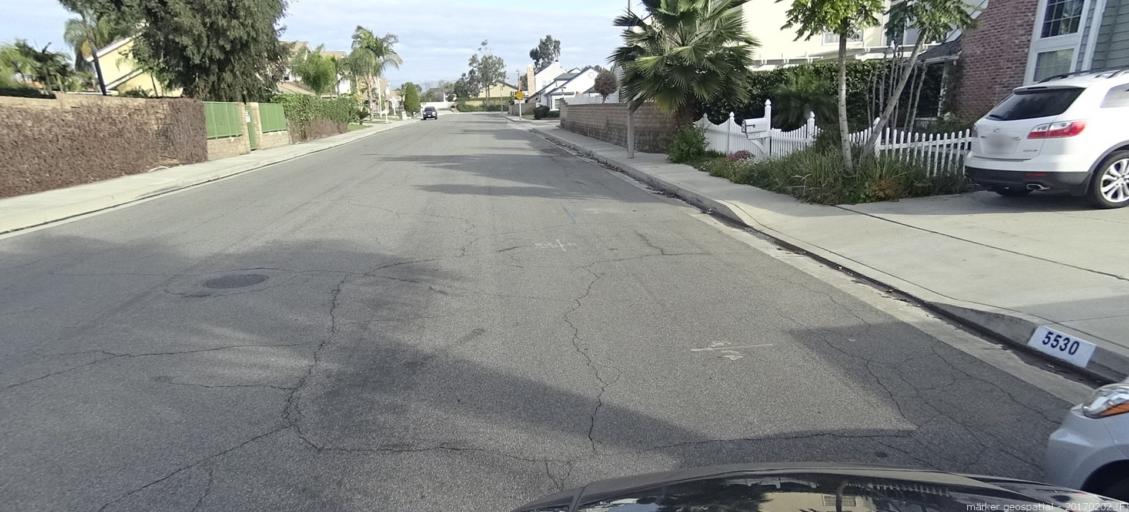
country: US
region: California
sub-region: Orange County
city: Yorba Linda
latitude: 33.8808
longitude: -117.8416
